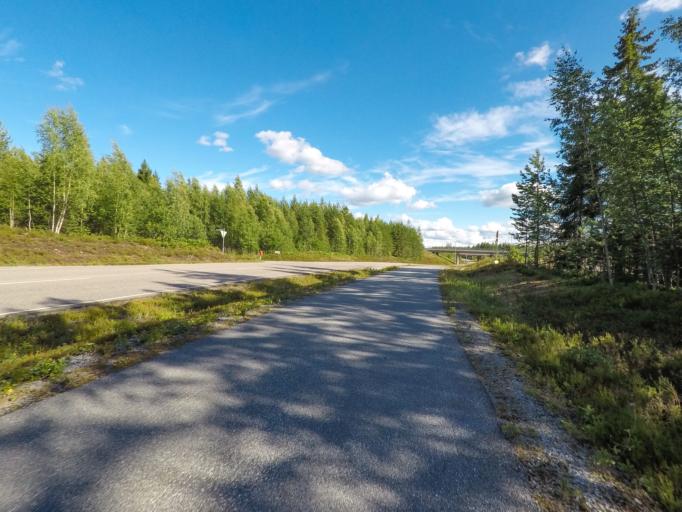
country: FI
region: South Karelia
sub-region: Lappeenranta
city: Joutseno
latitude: 61.1522
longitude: 28.6130
